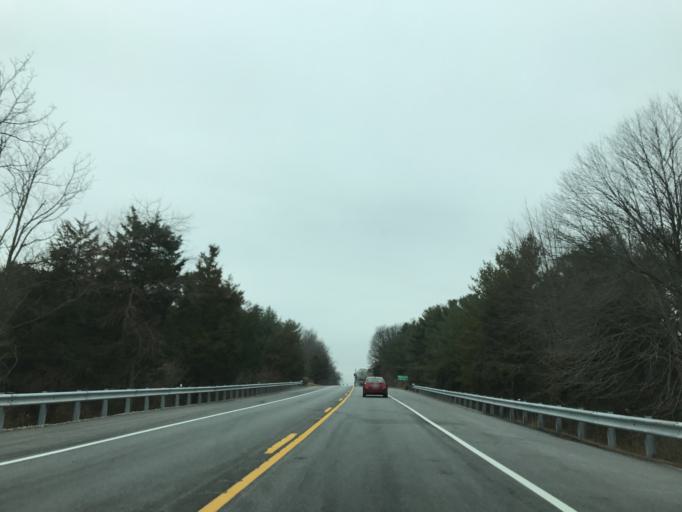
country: US
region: Maryland
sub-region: Carroll County
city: Taneytown
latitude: 39.6279
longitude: -77.1035
